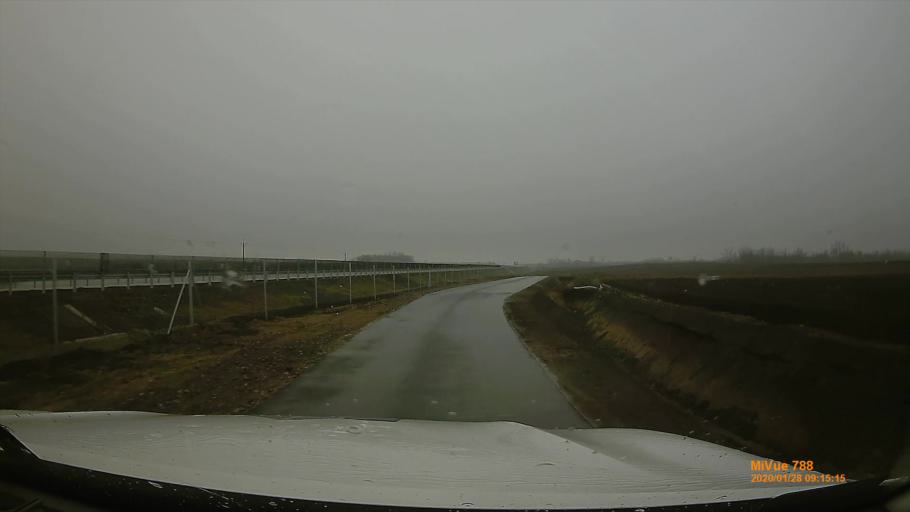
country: HU
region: Pest
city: Pilis
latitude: 47.2984
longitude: 19.5699
